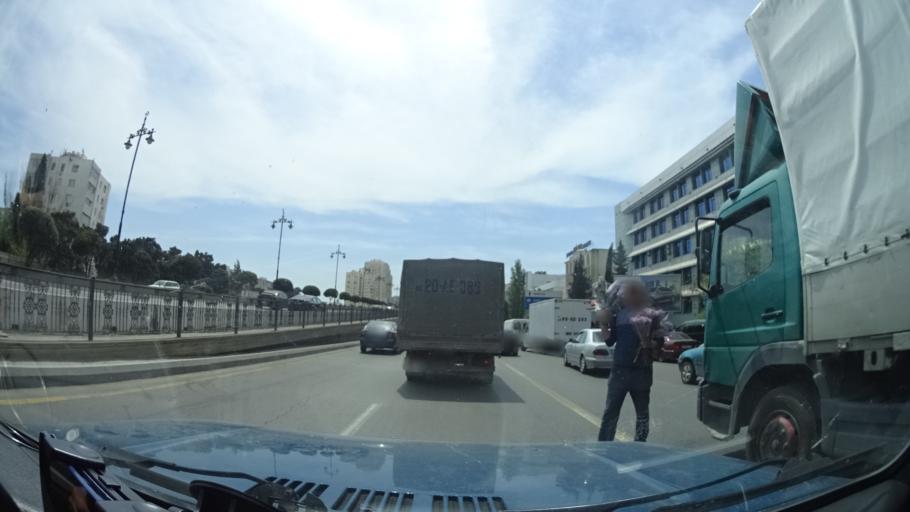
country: AZ
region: Baki
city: Khodzhi-Gasan
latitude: 40.4061
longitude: 49.8063
